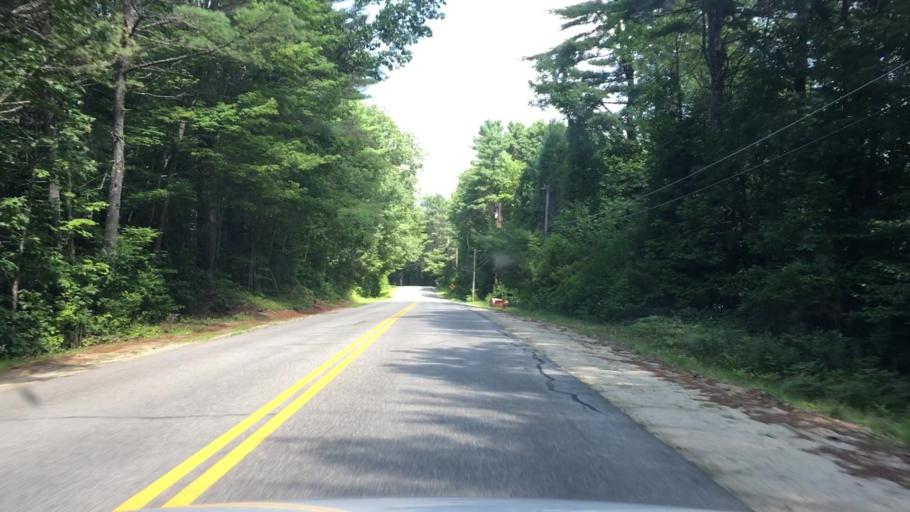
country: US
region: Maine
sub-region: Cumberland County
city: Raymond
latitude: 43.9297
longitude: -70.5214
